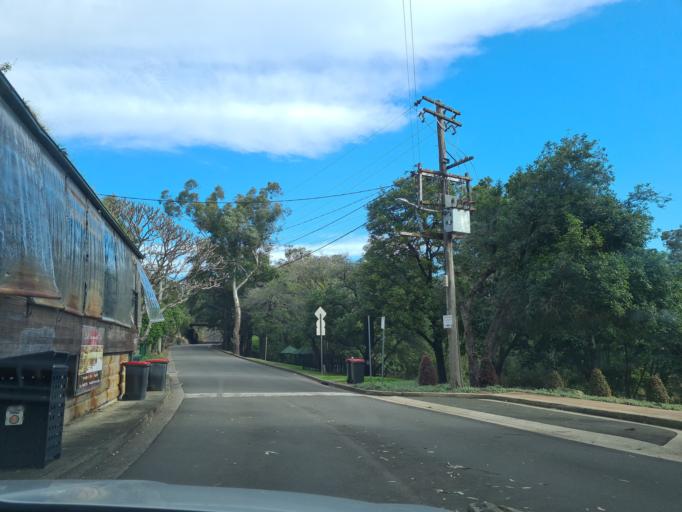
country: AU
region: New South Wales
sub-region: Parramatta
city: Northmead
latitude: -33.7913
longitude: 151.0074
